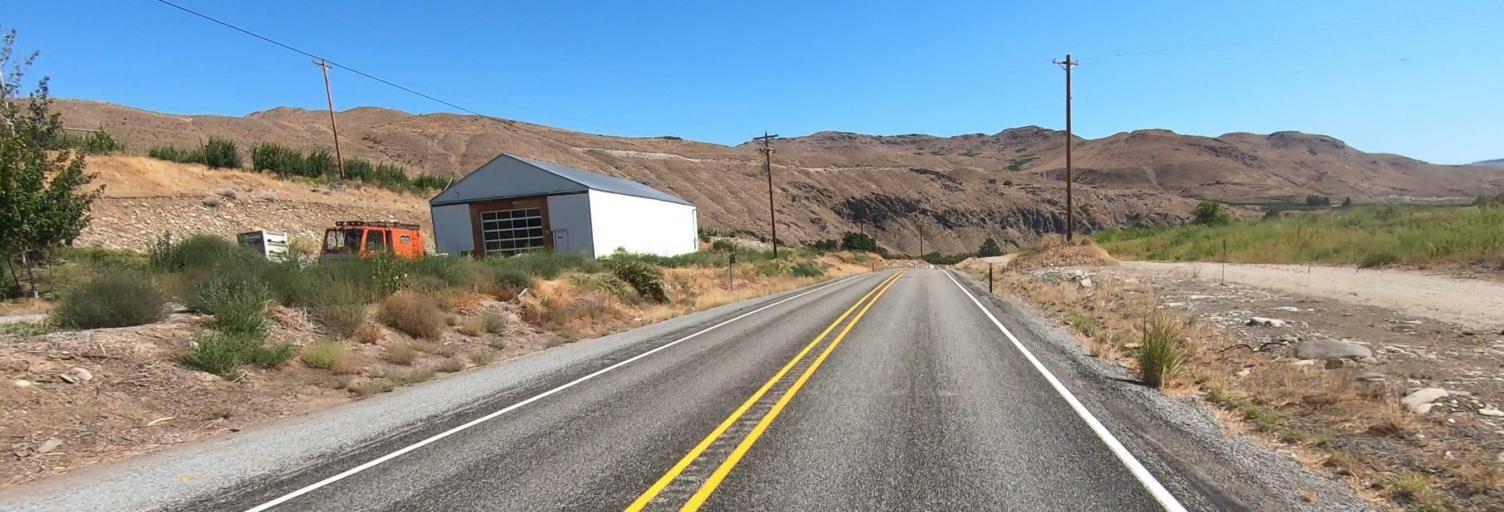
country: US
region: Washington
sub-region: Okanogan County
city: Brewster
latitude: 48.0762
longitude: -119.9635
